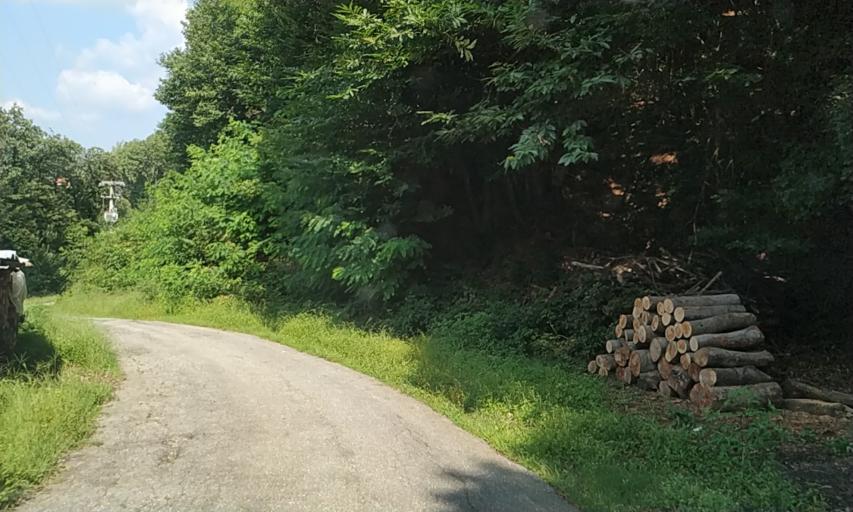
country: IT
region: Piedmont
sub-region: Provincia di Vercelli
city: Cellio
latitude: 45.7449
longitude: 8.3146
